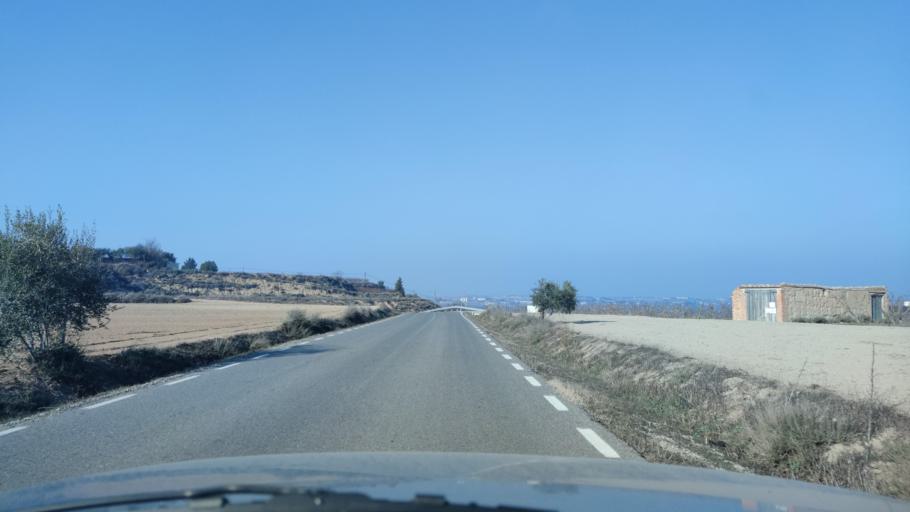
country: ES
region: Catalonia
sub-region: Provincia de Lleida
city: Sunyer
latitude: 41.5542
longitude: 0.5732
